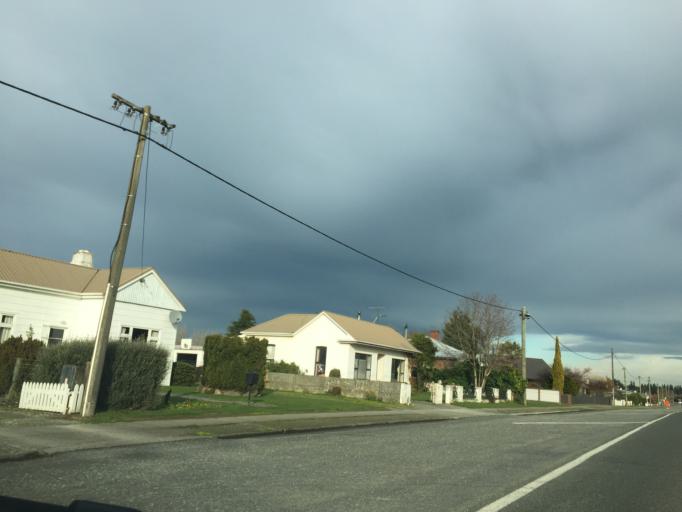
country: NZ
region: Southland
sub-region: Gore District
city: Gore
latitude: -46.1975
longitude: 168.8593
